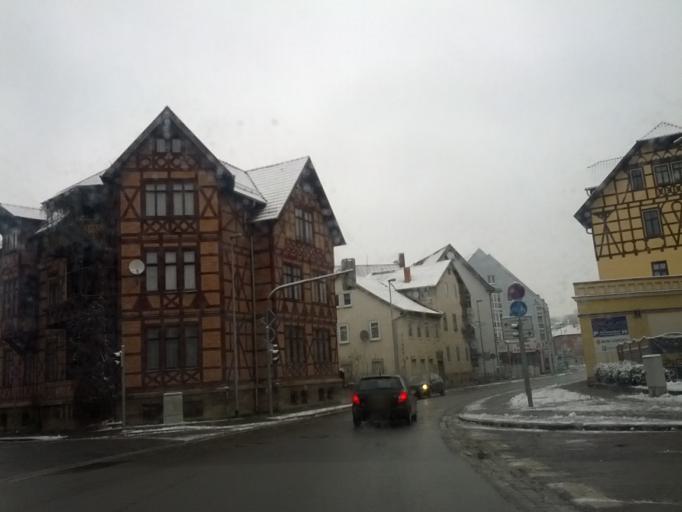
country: DE
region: Thuringia
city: Meiningen
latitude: 50.5763
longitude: 10.4164
